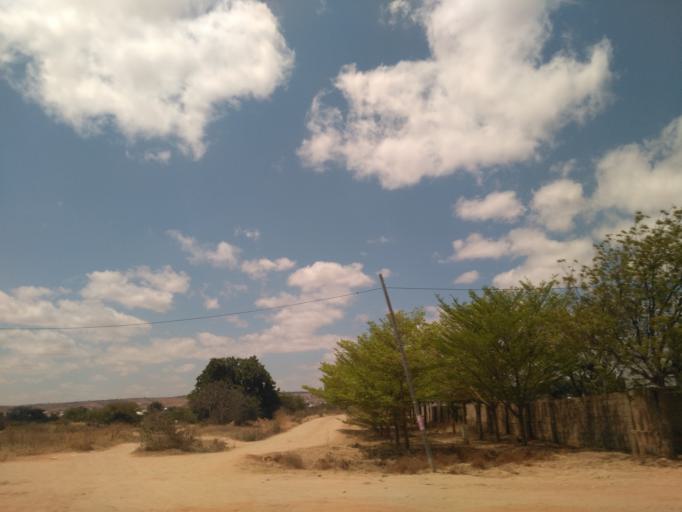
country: TZ
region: Dodoma
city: Kisasa
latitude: -6.1680
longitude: 35.7793
